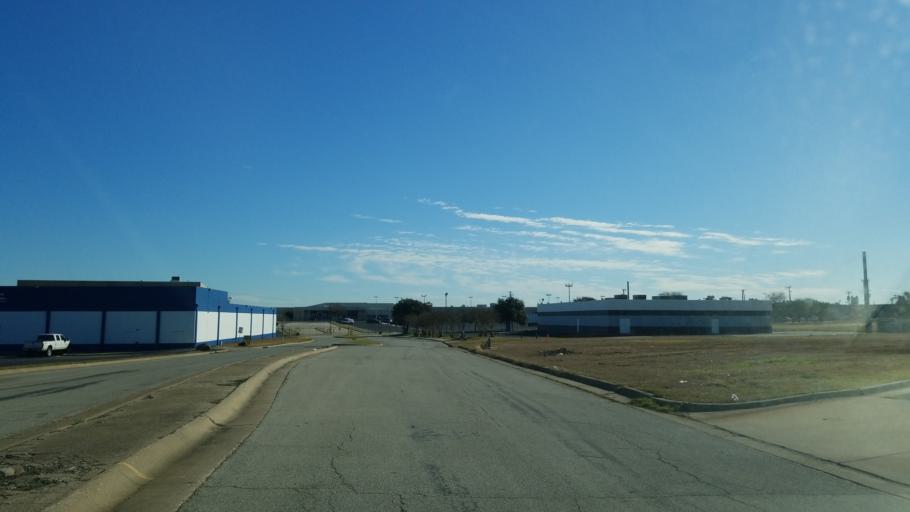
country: US
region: Texas
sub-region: Dallas County
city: Grand Prairie
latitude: 32.7431
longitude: -97.0528
